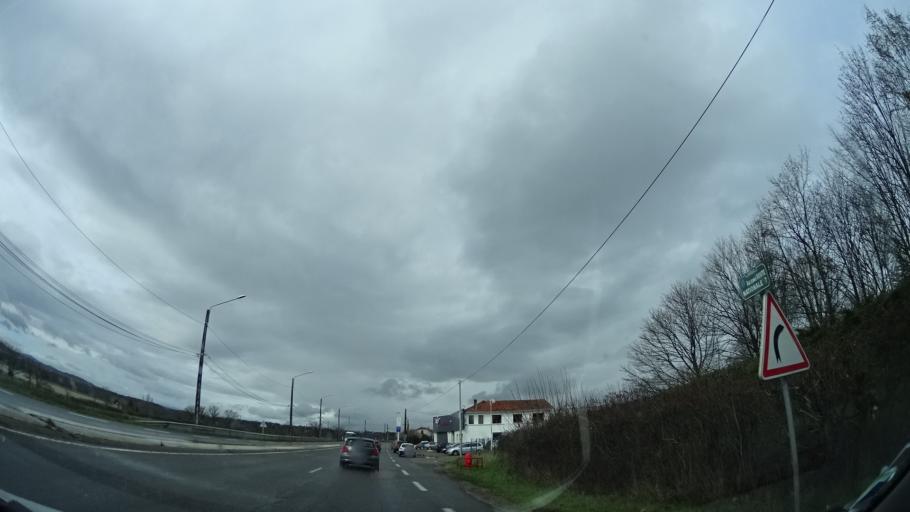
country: FR
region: Rhone-Alpes
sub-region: Departement du Rhone
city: Charbonnieres-les-Bains
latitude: 45.7907
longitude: 4.7432
